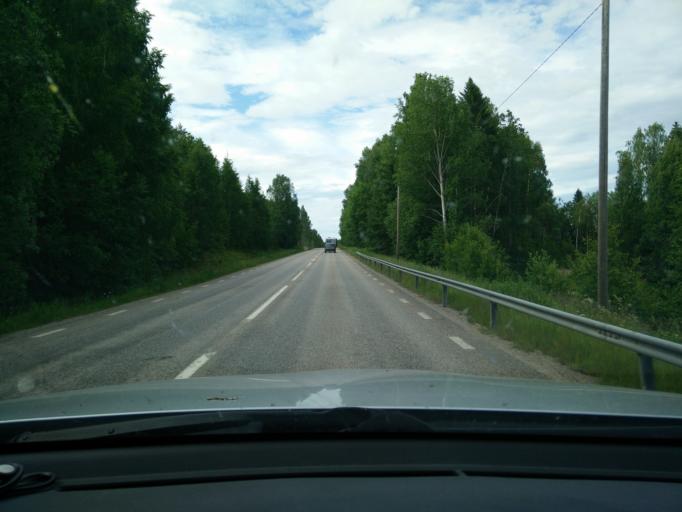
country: SE
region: Gaevleborg
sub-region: Nordanstigs Kommun
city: Bergsjoe
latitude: 61.9596
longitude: 17.0625
